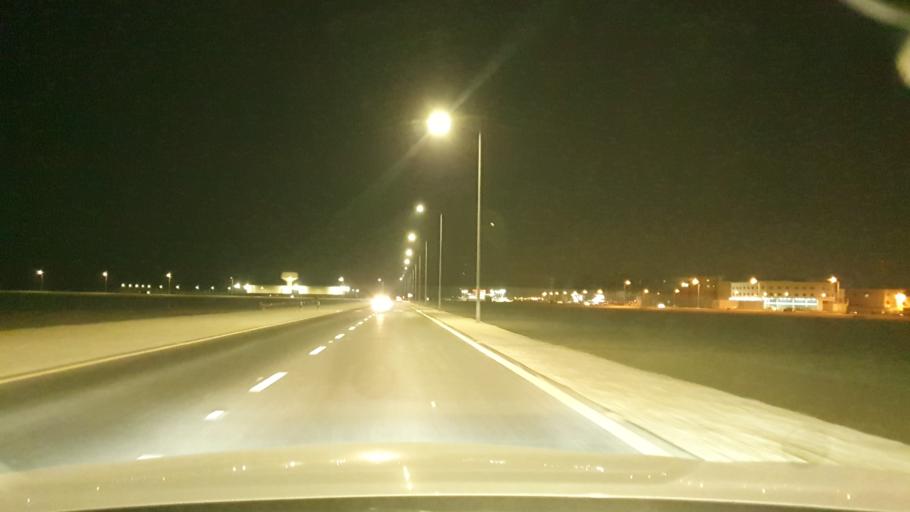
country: BH
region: Muharraq
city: Al Muharraq
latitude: 26.2757
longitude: 50.5924
